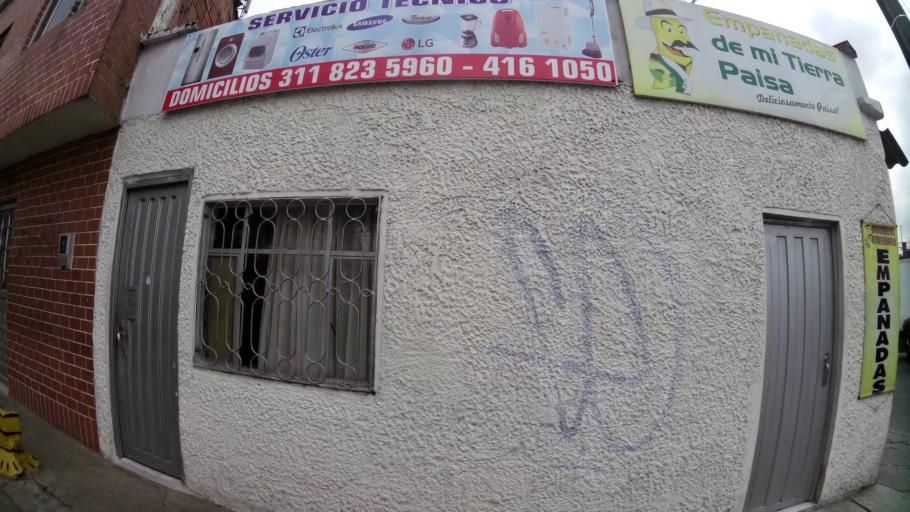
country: CO
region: Bogota D.C.
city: Bogota
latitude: 4.6719
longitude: -74.1249
